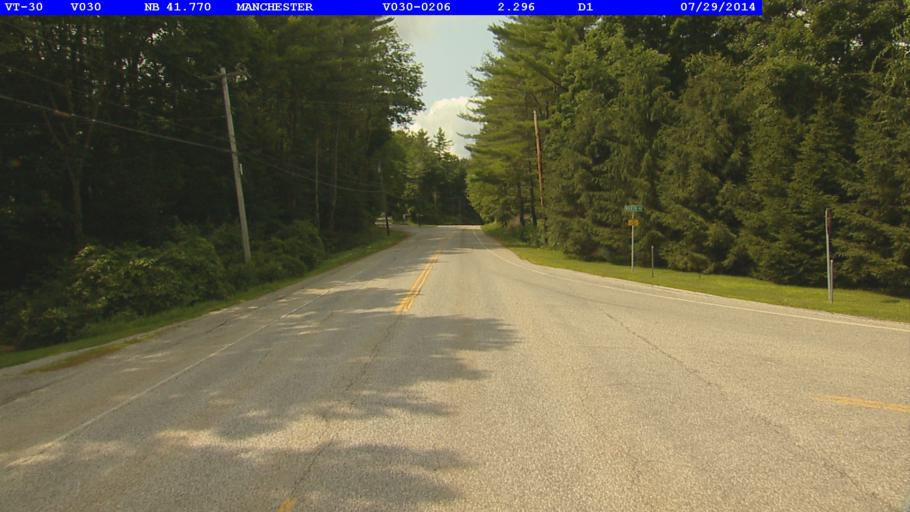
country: US
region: Vermont
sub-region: Bennington County
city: Manchester Center
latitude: 43.2069
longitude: -73.0616
